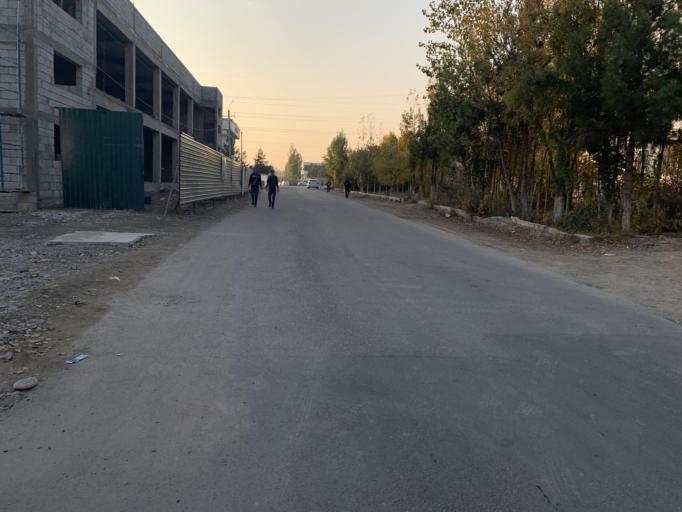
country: UZ
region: Namangan
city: Namangan Shahri
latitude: 41.0025
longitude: 71.6050
